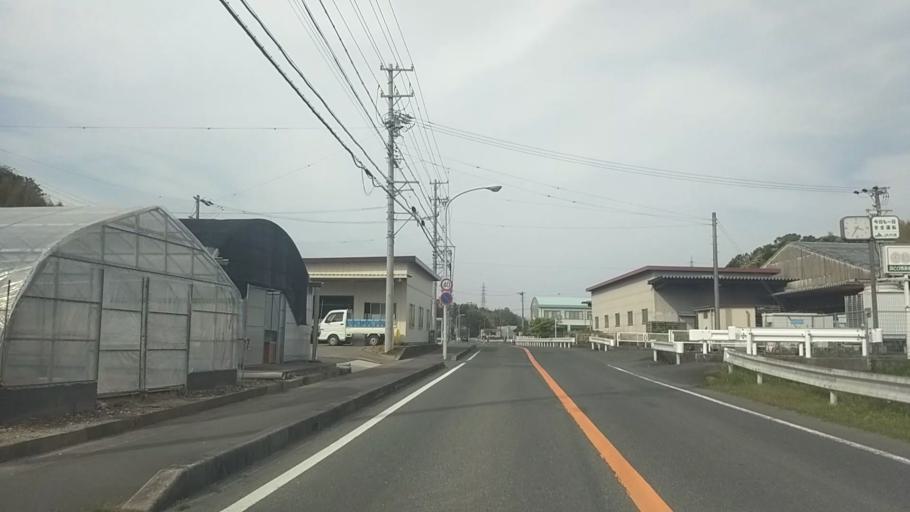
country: JP
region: Shizuoka
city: Hamamatsu
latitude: 34.7159
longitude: 137.6507
